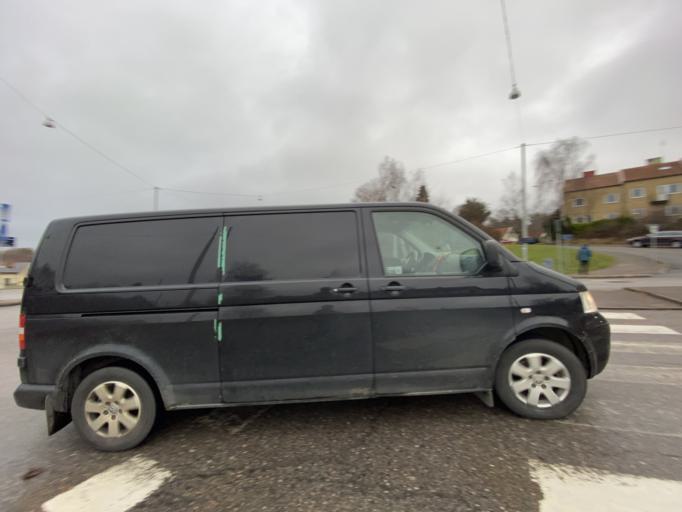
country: SE
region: Vaestra Goetaland
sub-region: Goteborg
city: Eriksbo
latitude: 57.7175
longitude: 12.0412
